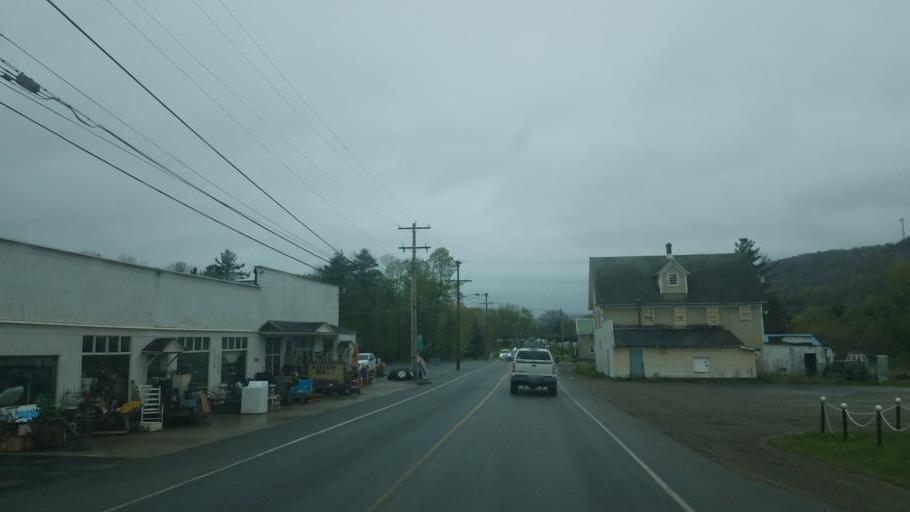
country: US
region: Pennsylvania
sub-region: McKean County
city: Smethport
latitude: 41.8099
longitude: -78.4260
